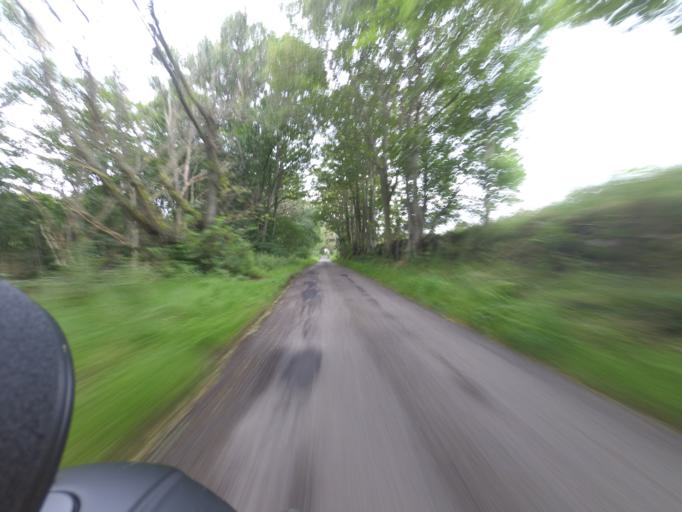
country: GB
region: Scotland
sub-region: Highland
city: Muir of Ord
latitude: 57.5123
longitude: -4.3851
